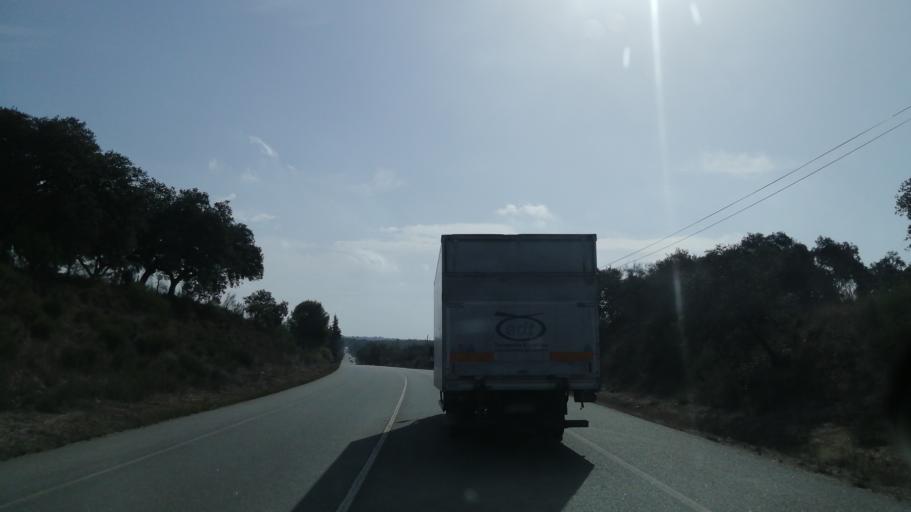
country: PT
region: Evora
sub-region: Montemor-O-Novo
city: Montemor-o-Novo
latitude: 38.6222
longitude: -8.0939
